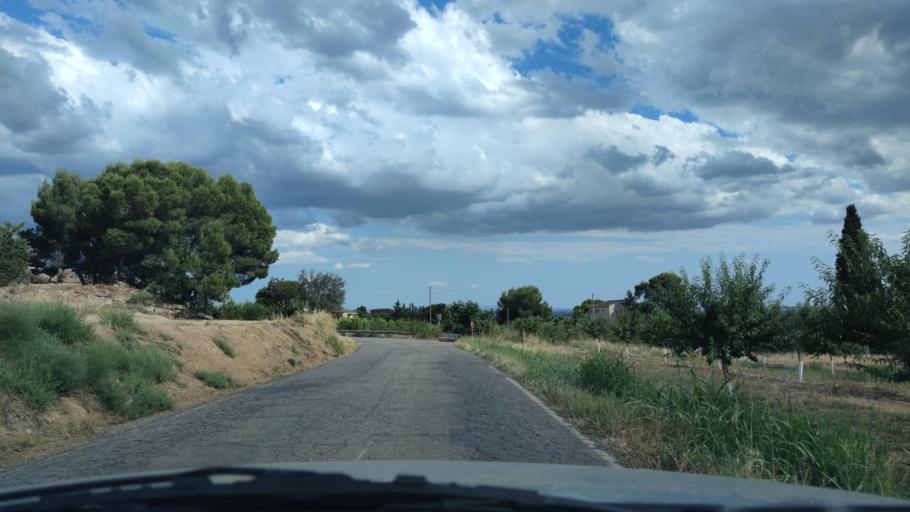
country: ES
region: Catalonia
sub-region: Provincia de Lleida
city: Lleida
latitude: 41.6028
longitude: 0.5864
